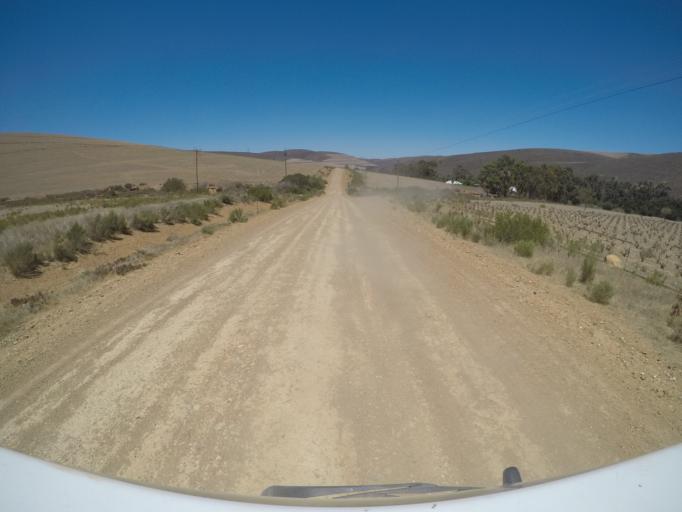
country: ZA
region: Western Cape
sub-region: Overberg District Municipality
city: Caledon
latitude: -34.1302
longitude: 19.2405
